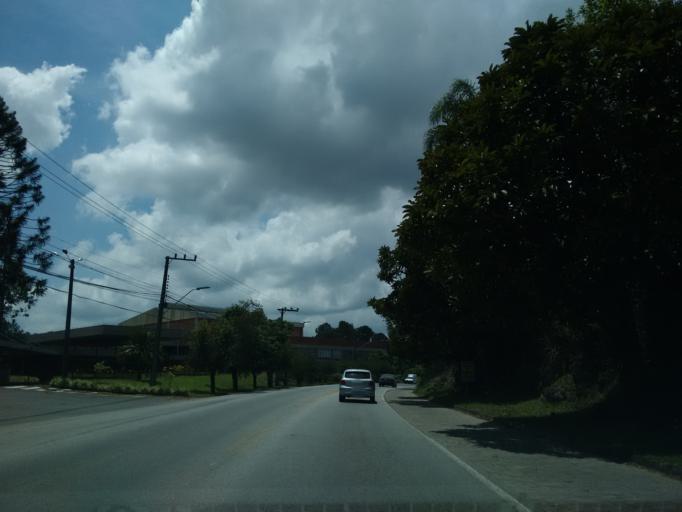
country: BR
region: Santa Catarina
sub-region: Blumenau
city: Blumenau
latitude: -26.9028
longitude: -49.0148
